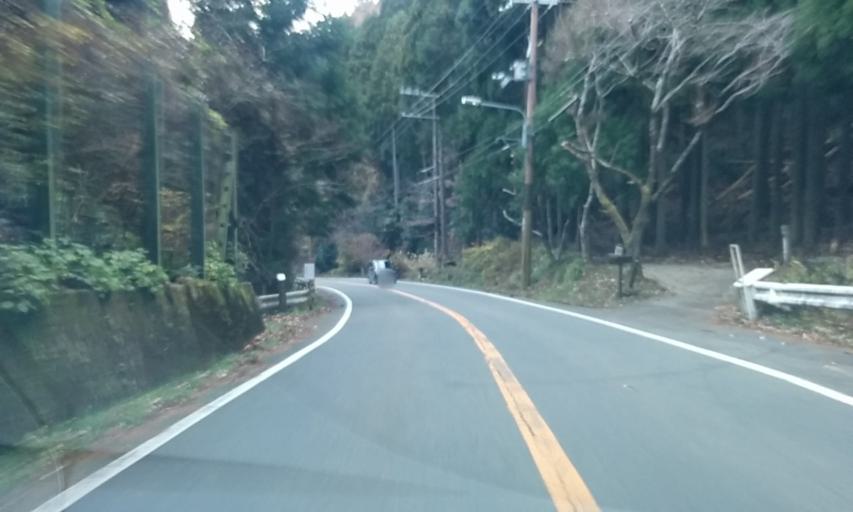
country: JP
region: Kyoto
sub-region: Kyoto-shi
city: Kamigyo-ku
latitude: 35.1118
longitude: 135.8086
